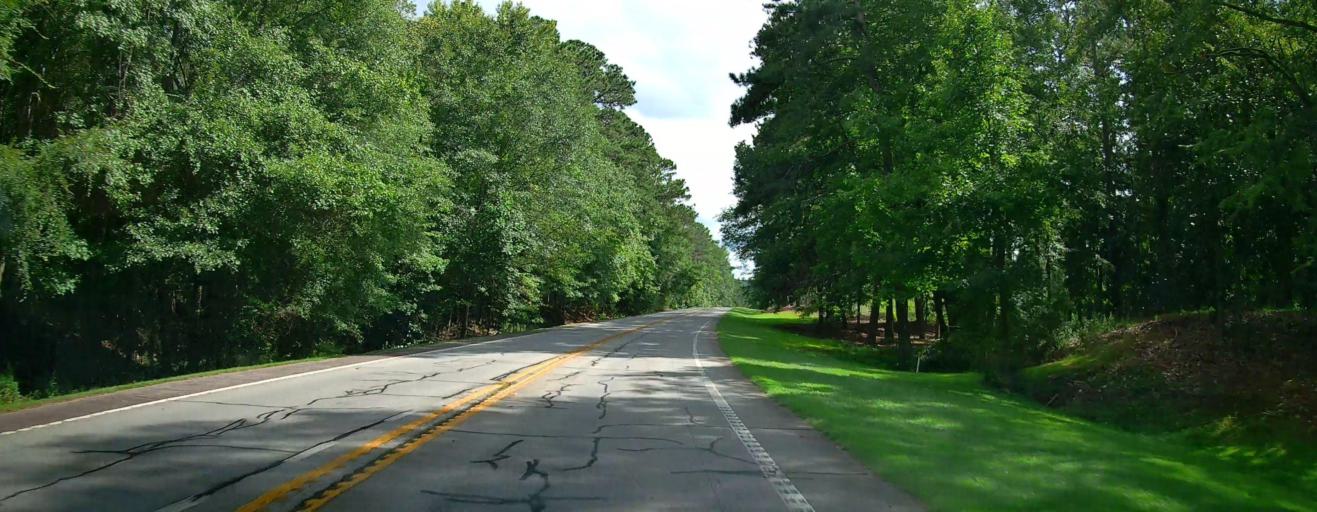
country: US
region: Georgia
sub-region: Harris County
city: Pine Mountain
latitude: 32.8440
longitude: -84.8435
